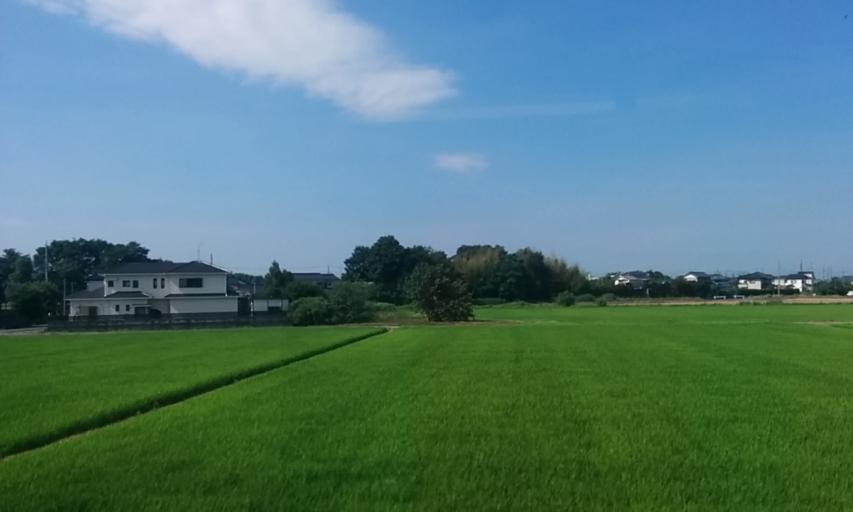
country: JP
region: Saitama
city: Kazo
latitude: 36.1419
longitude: 139.5680
